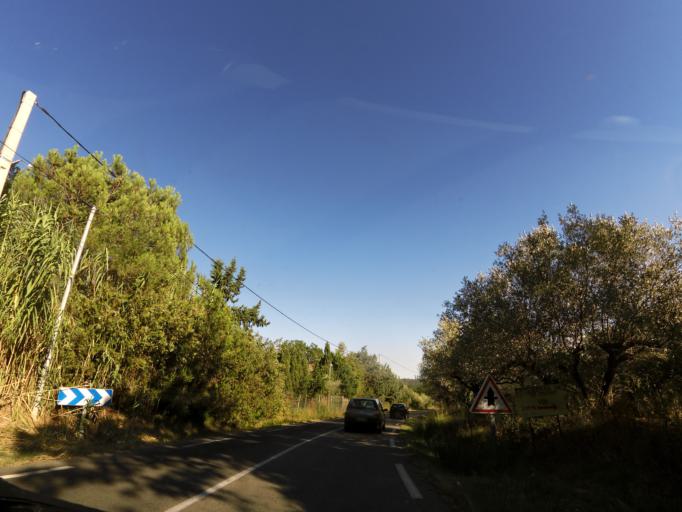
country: FR
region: Languedoc-Roussillon
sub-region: Departement du Gard
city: Quissac
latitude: 43.8426
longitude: 4.0283
